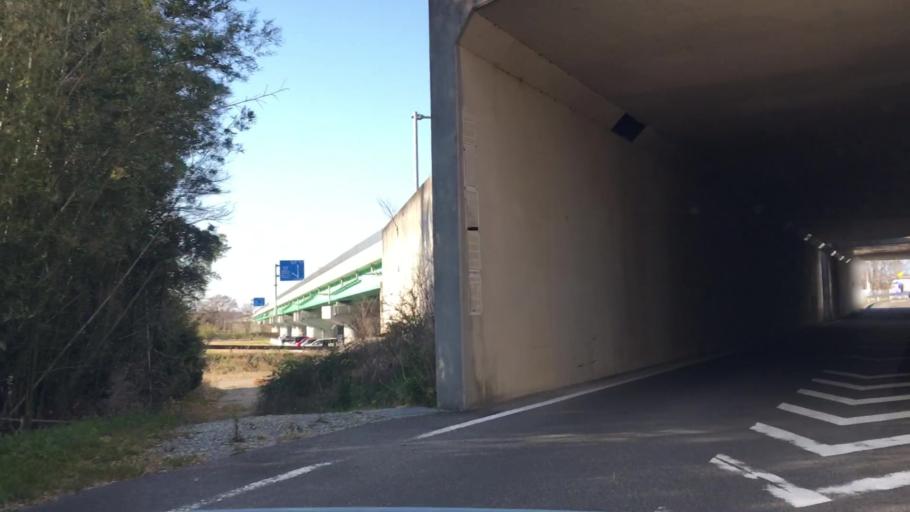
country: JP
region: Aichi
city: Nishio
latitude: 34.8759
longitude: 137.0813
